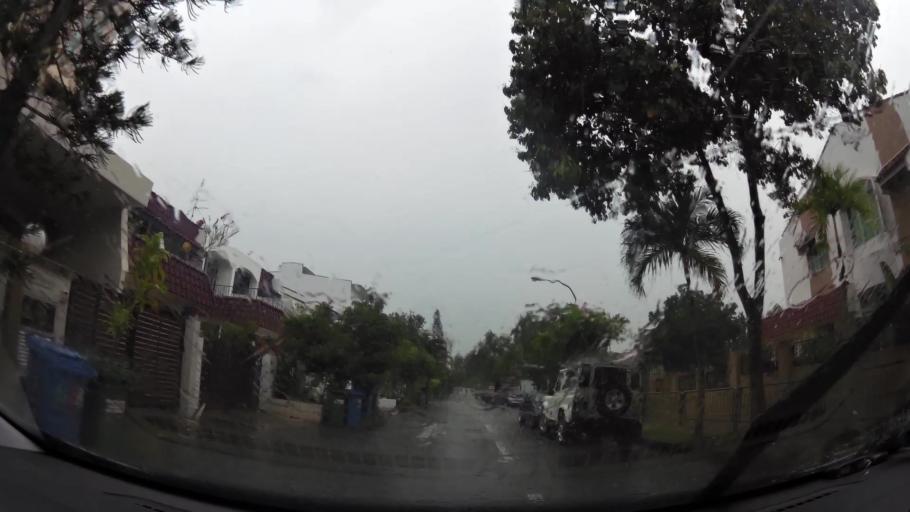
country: MY
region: Johor
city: Kampung Pasir Gudang Baru
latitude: 1.3881
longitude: 103.8565
